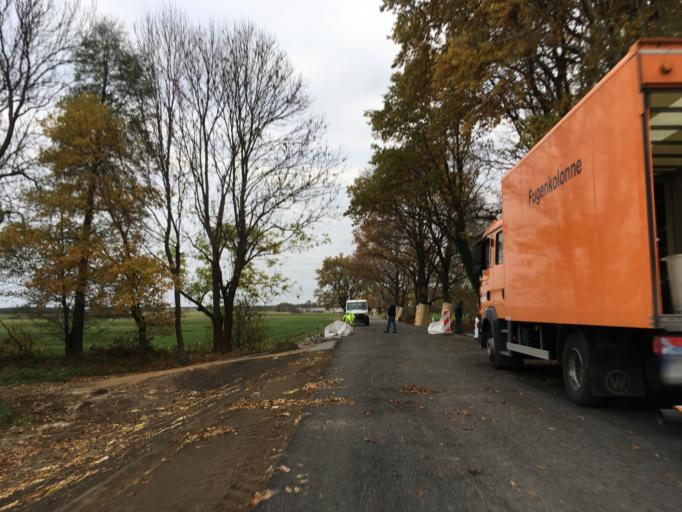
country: DE
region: Brandenburg
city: Calau
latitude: 51.7642
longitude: 13.9880
